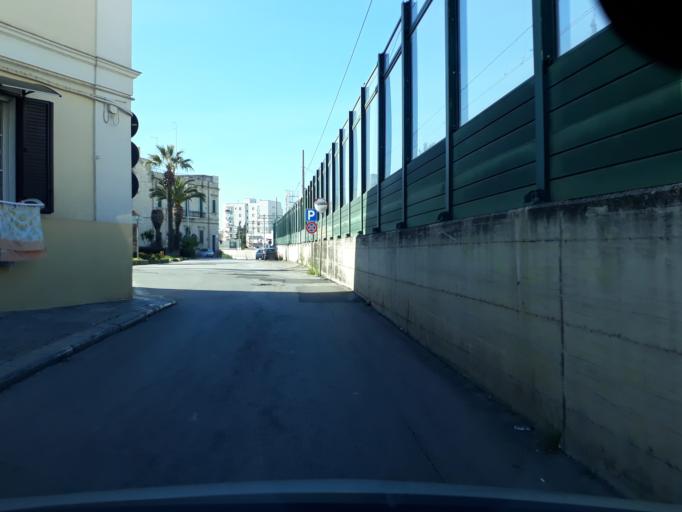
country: IT
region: Apulia
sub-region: Provincia di Bari
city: Monopoli
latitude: 40.9487
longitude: 17.2987
